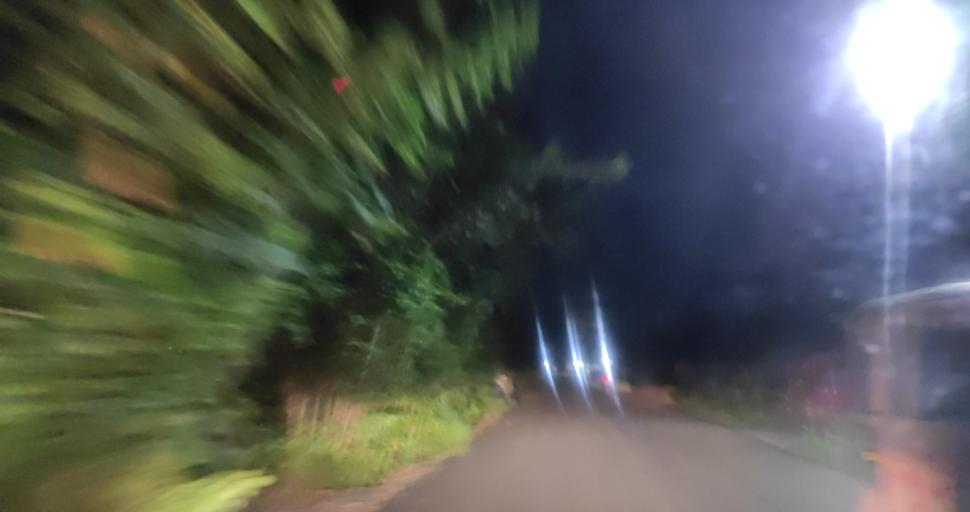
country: IN
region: Kerala
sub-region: Alappuzha
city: Vayalar
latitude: 9.6802
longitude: 76.3033
